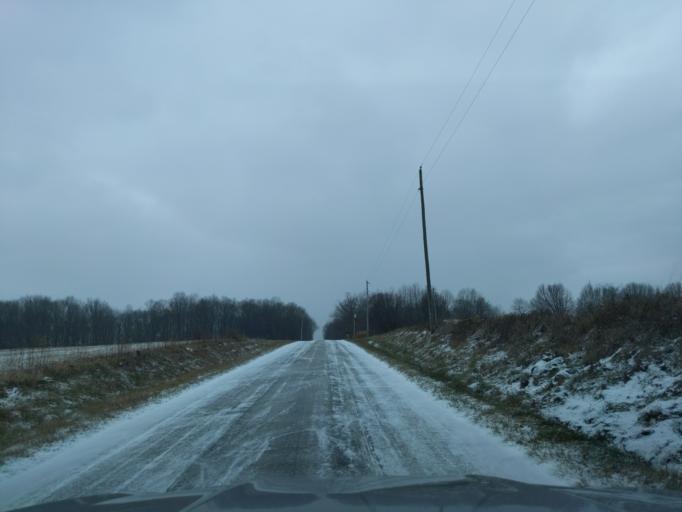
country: US
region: Indiana
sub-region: Decatur County
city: Greensburg
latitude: 39.2340
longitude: -85.4836
